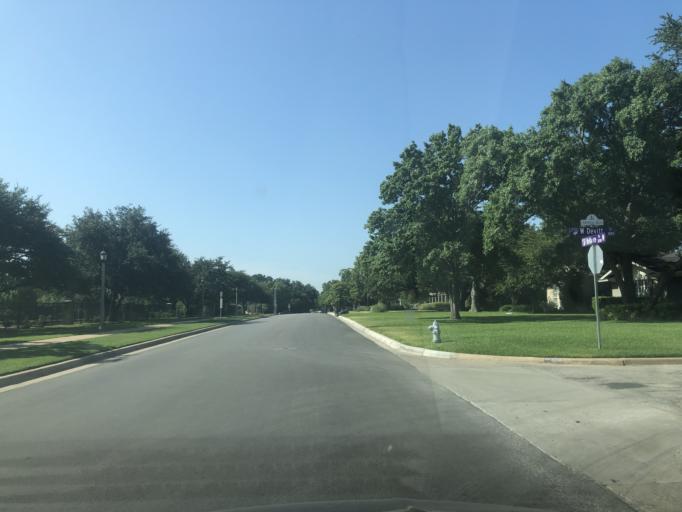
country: US
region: Texas
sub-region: Tarrant County
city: Edgecliff Village
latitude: 32.7036
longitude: -97.3746
